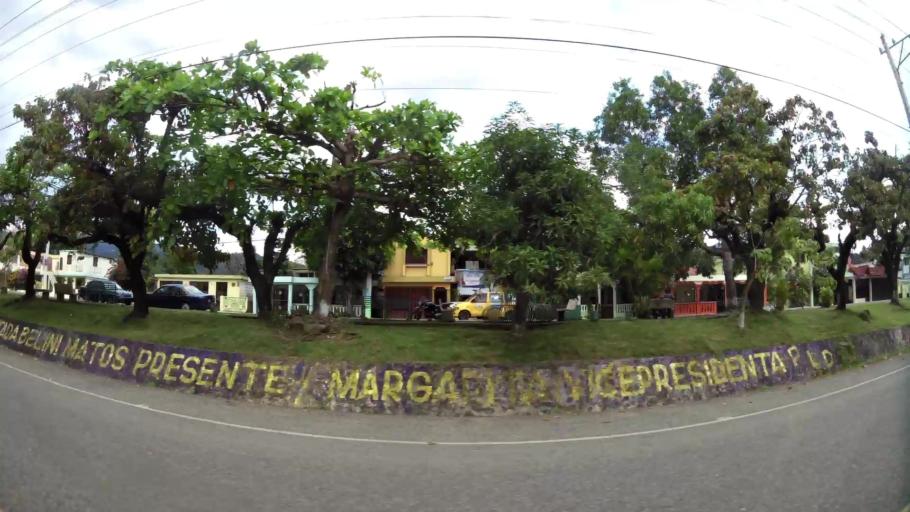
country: DO
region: San Cristobal
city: Villa Altagracia
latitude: 18.6823
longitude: -70.1790
